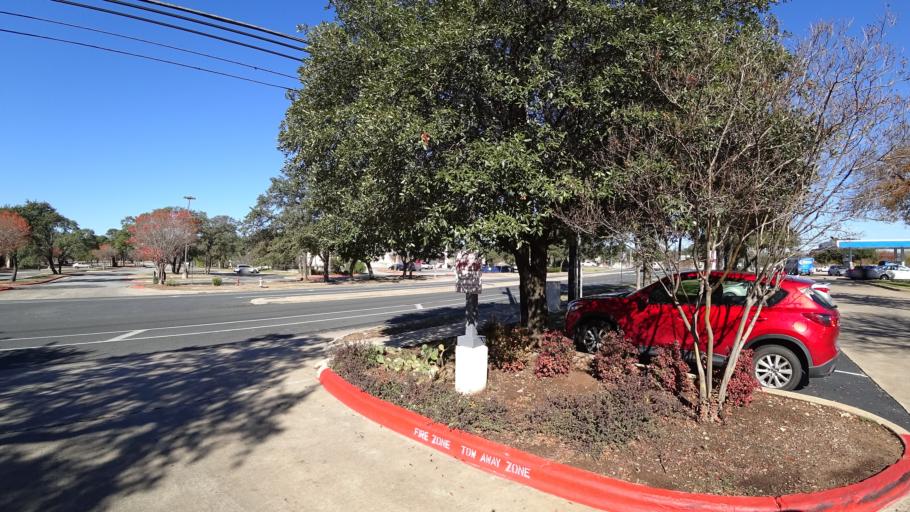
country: US
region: Texas
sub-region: Travis County
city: Wells Branch
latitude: 30.4236
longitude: -97.7140
